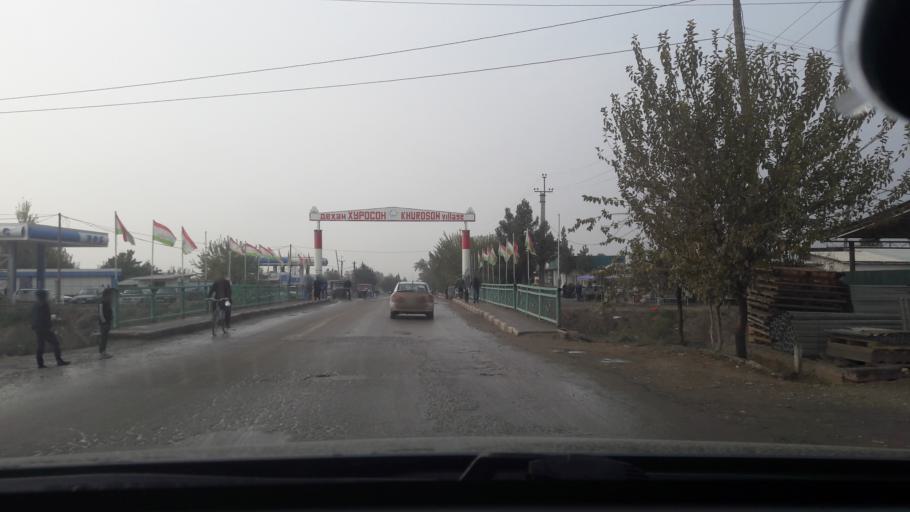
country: TJ
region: Khatlon
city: Abdurahmoni Jomi
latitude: 37.9867
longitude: 68.7032
